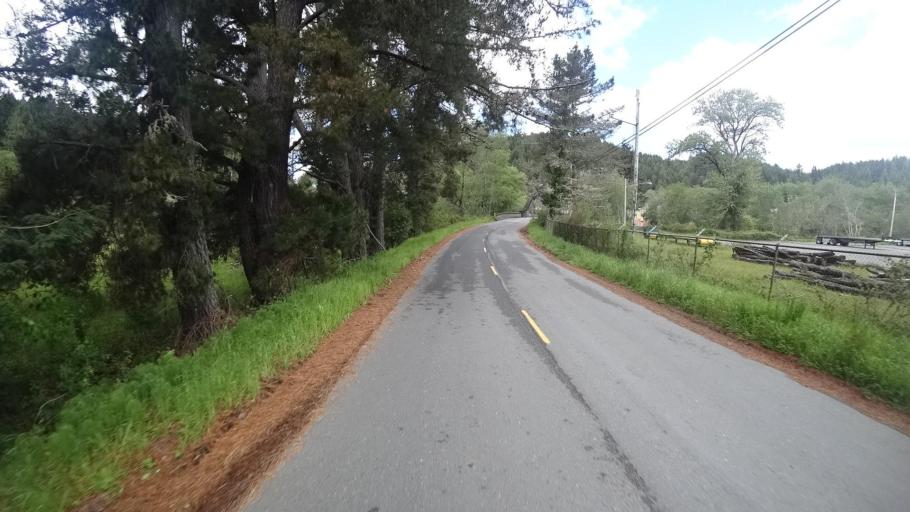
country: US
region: California
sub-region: Humboldt County
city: Blue Lake
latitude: 40.8700
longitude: -123.9601
